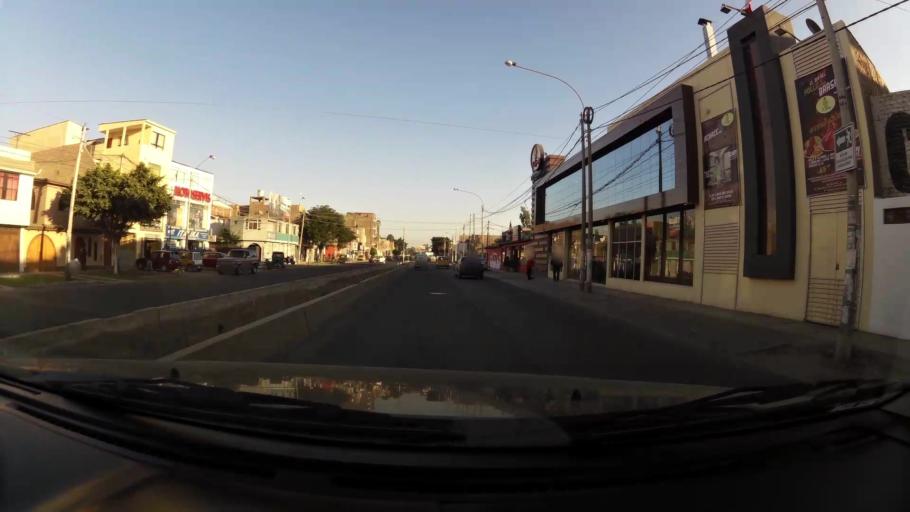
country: PE
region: Ica
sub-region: Provincia de Ica
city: Ica
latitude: -14.0676
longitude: -75.7354
